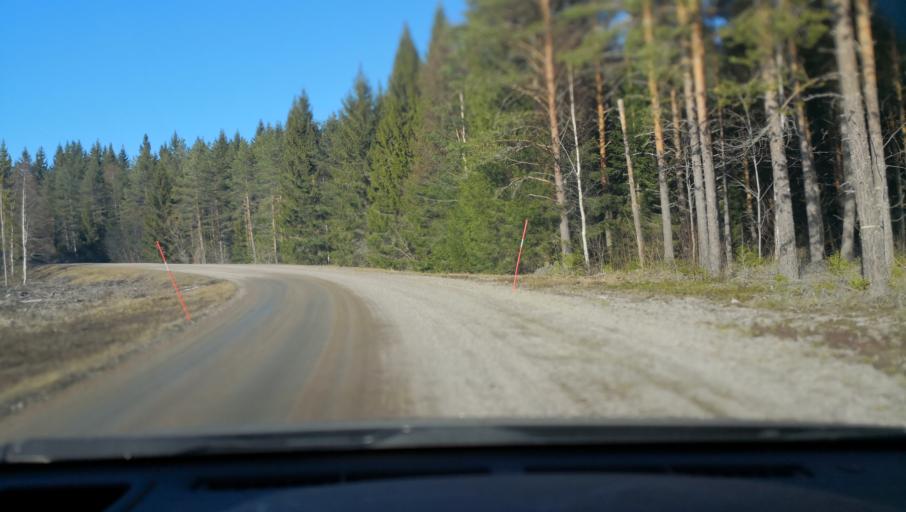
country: SE
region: Vaestmanland
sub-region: Sala Kommun
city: Sala
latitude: 60.1653
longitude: 16.6355
